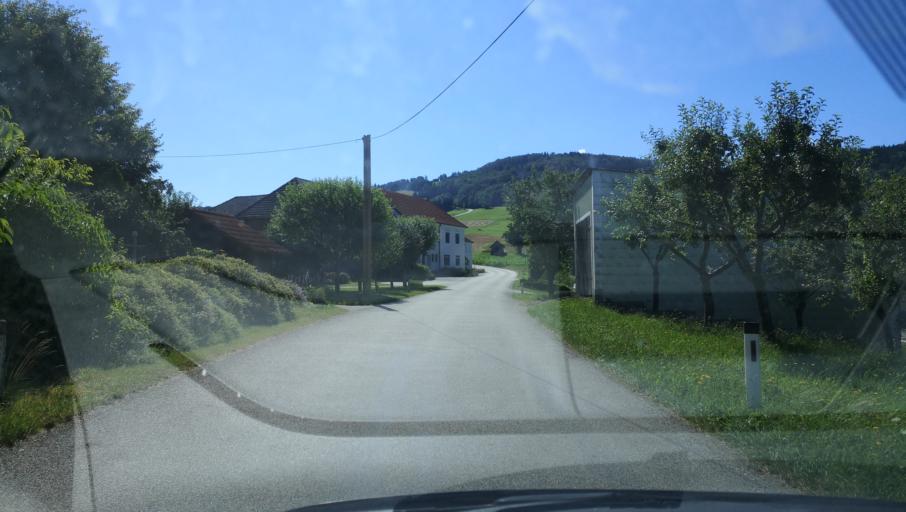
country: AT
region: Lower Austria
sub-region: Politischer Bezirk Amstetten
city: Euratsfeld
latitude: 48.0444
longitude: 14.9215
